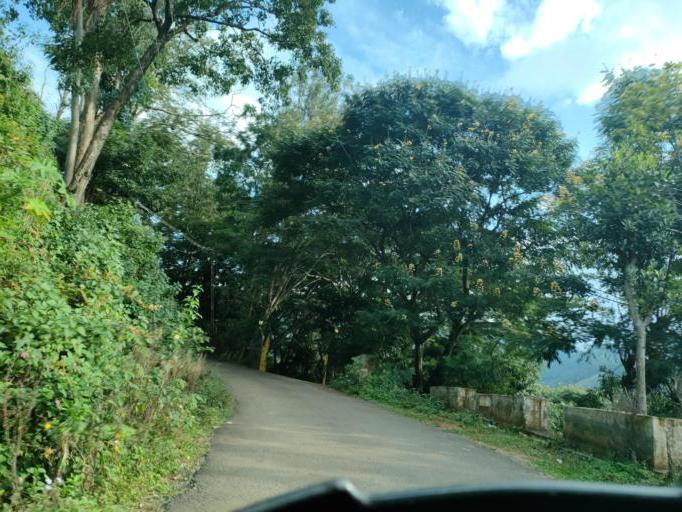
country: IN
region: Tamil Nadu
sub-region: Dindigul
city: Kodaikanal
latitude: 10.2797
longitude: 77.5293
